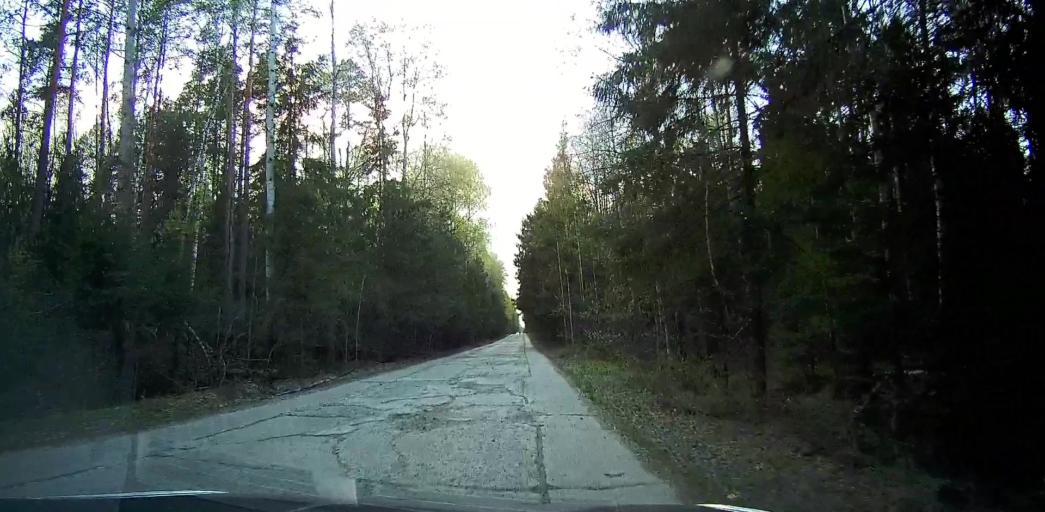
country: RU
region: Moskovskaya
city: Malyshevo
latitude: 55.5361
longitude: 38.3868
